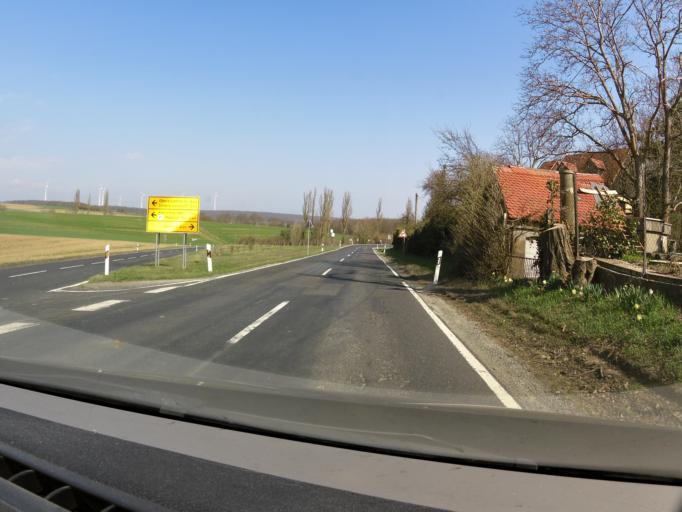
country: DE
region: Bavaria
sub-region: Regierungsbezirk Unterfranken
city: Prosselsheim
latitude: 49.8682
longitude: 10.1511
